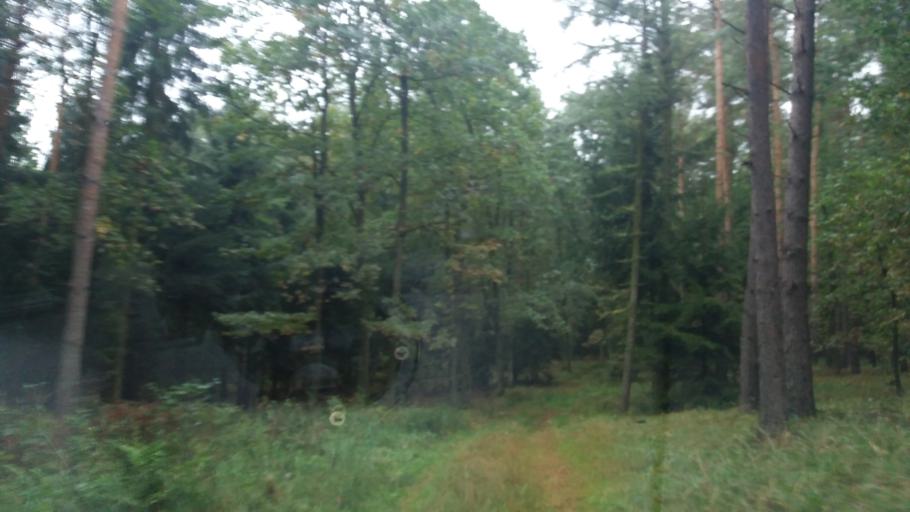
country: PL
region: West Pomeranian Voivodeship
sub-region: Powiat choszczenski
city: Pelczyce
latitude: 53.0729
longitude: 15.2876
